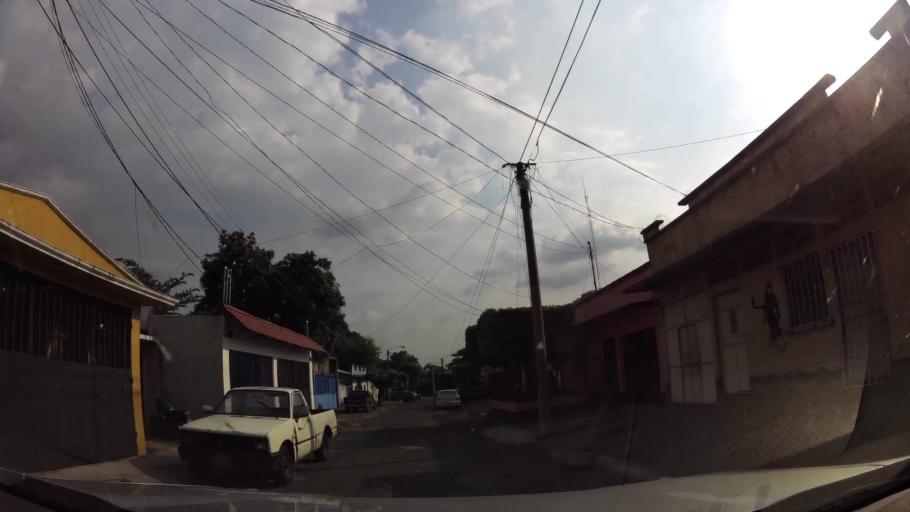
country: GT
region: Escuintla
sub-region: Municipio de Escuintla
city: Escuintla
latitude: 14.3171
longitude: -90.7942
